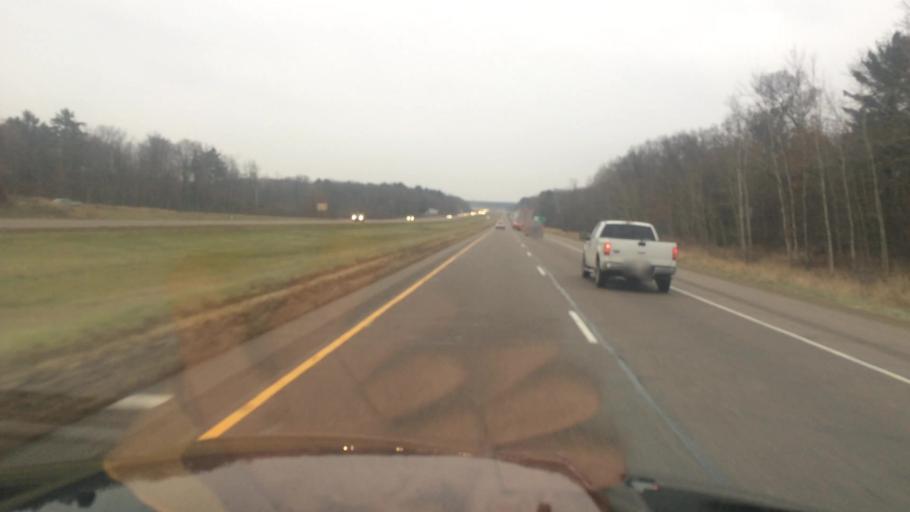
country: US
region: Wisconsin
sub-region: Portage County
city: Stevens Point
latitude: 44.5898
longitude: -89.6109
